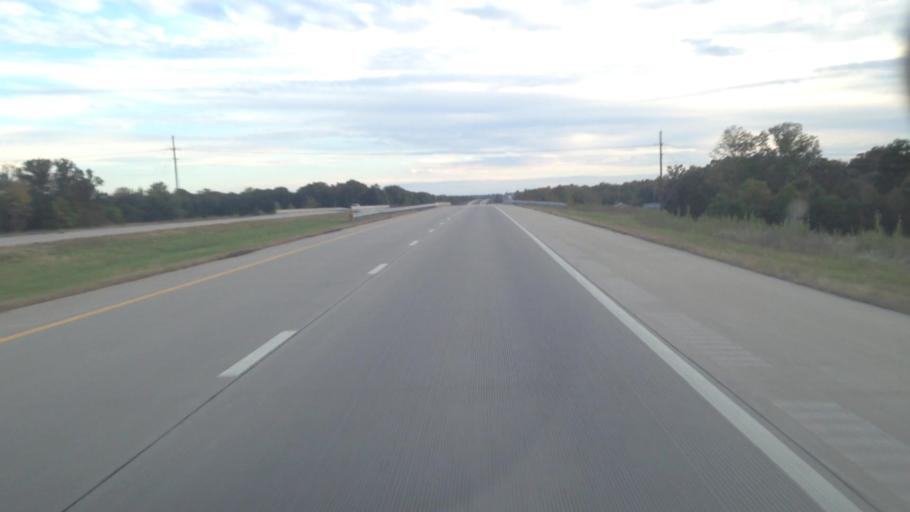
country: US
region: Kansas
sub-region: Douglas County
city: Baldwin City
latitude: 38.7621
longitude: -95.2684
